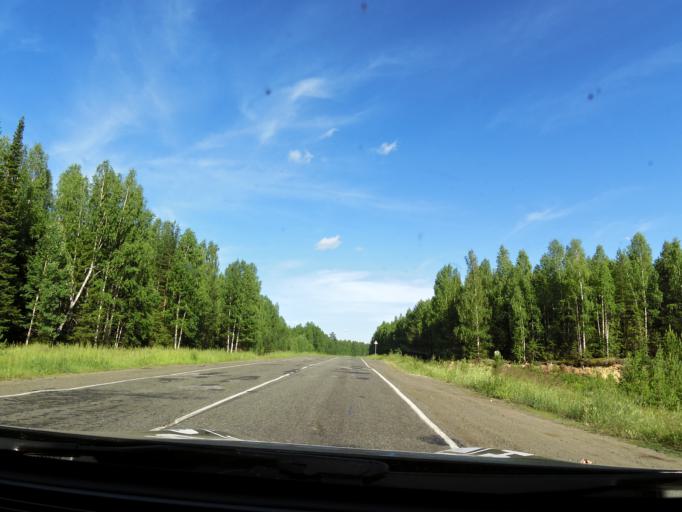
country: RU
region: Kirov
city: Dubrovka
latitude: 58.8986
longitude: 51.3108
